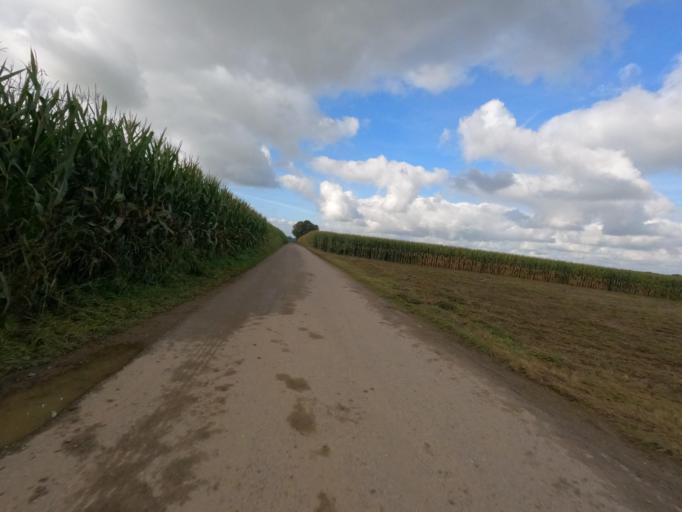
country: DE
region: North Rhine-Westphalia
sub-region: Regierungsbezirk Koln
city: Linnich
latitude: 51.0146
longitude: 6.2843
